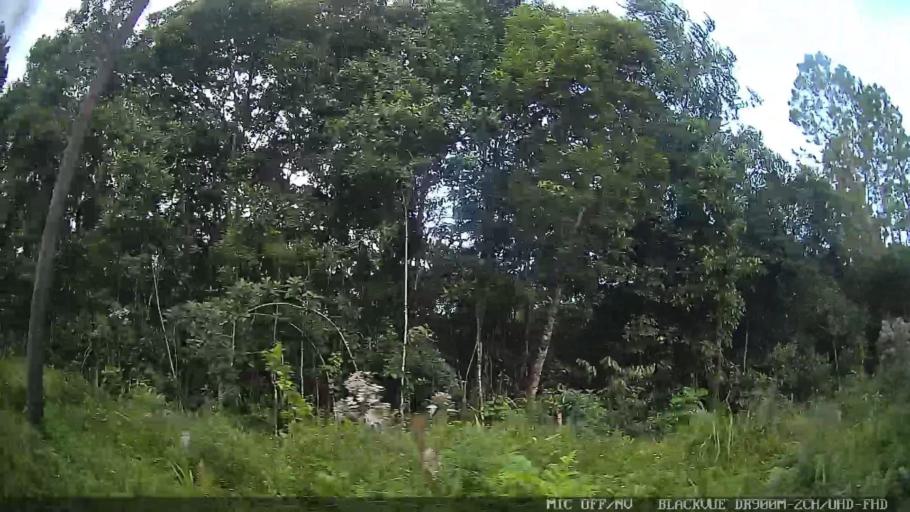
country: BR
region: Sao Paulo
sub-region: Peruibe
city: Peruibe
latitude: -24.1966
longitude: -46.9410
